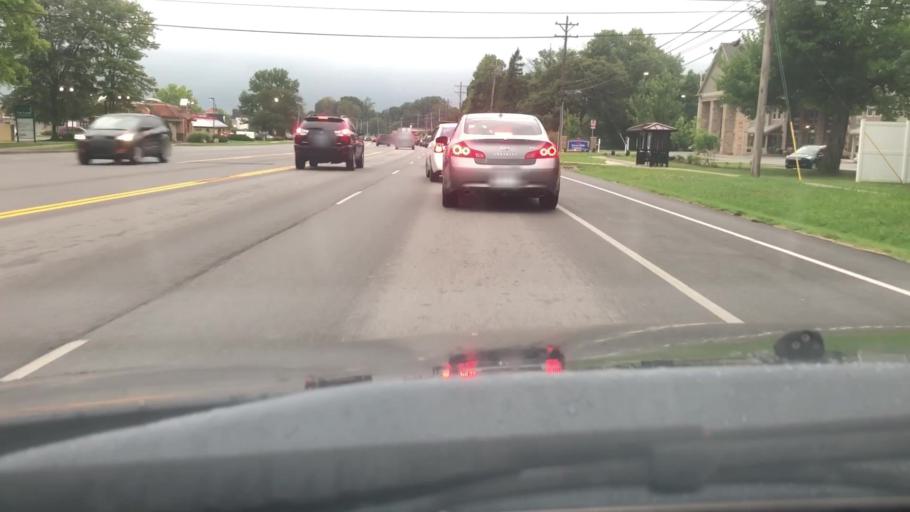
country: US
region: Kentucky
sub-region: Jefferson County
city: Hurstbourne Acres
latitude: 38.2127
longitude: -85.5876
